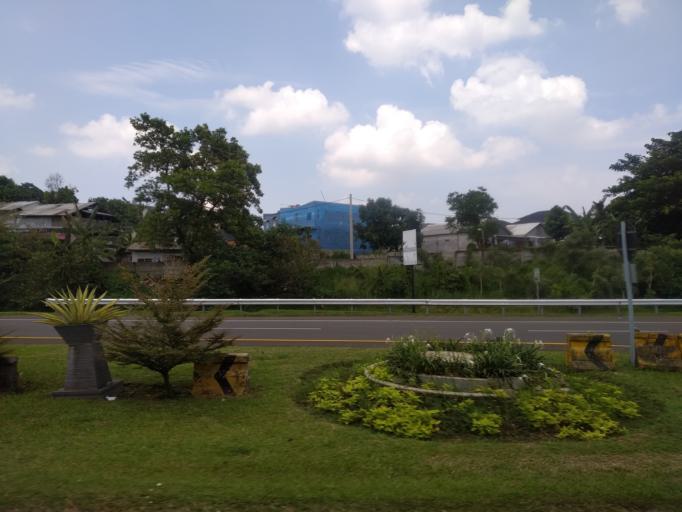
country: ID
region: West Java
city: Bogor
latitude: -6.5991
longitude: 106.8150
